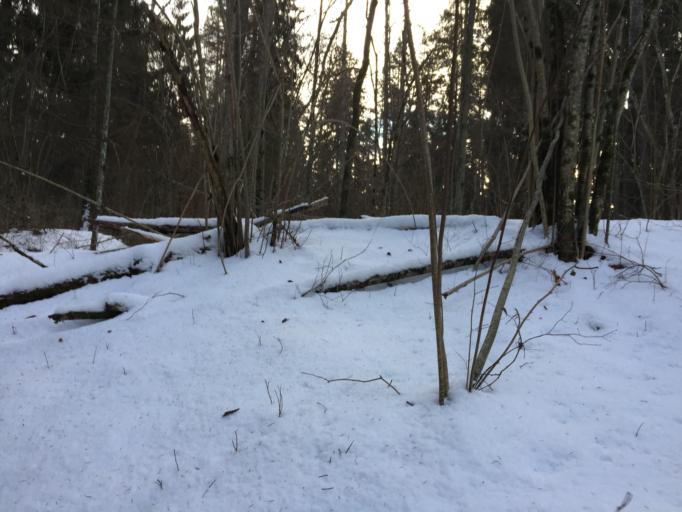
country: LV
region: Lielvarde
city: Lielvarde
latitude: 56.7055
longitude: 24.7945
